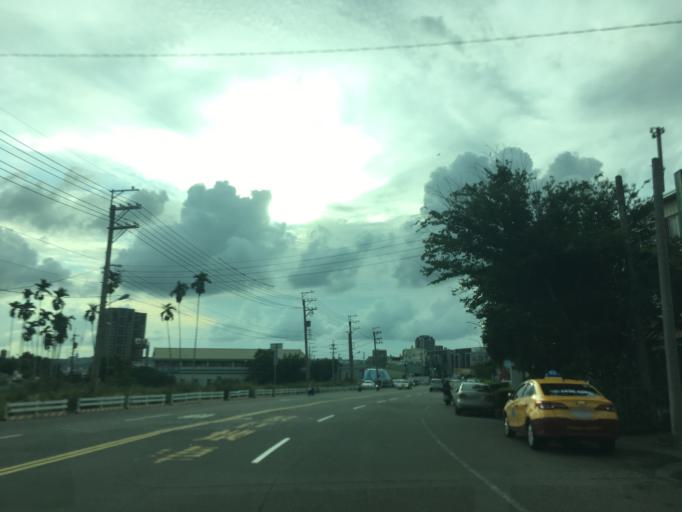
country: TW
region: Taiwan
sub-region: Taichung City
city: Taichung
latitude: 24.1364
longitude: 120.6345
